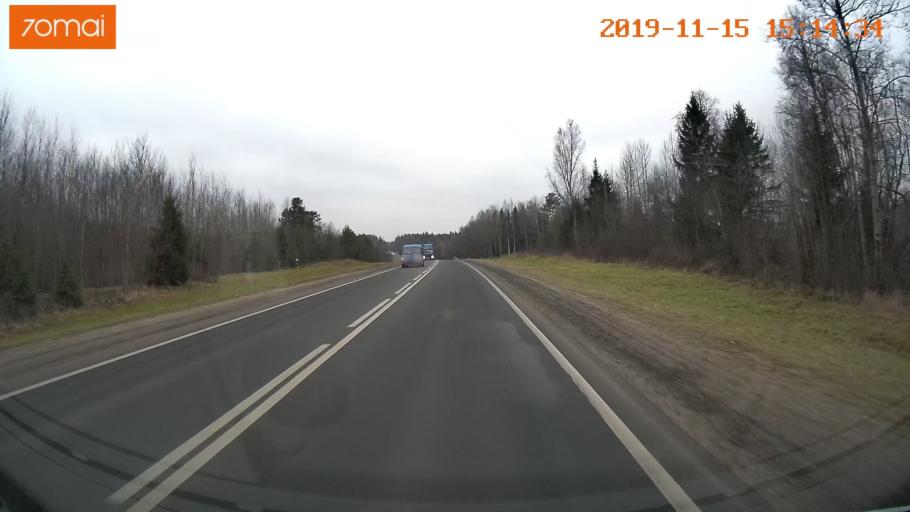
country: RU
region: Jaroslavl
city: Danilov
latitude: 58.2981
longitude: 40.2038
